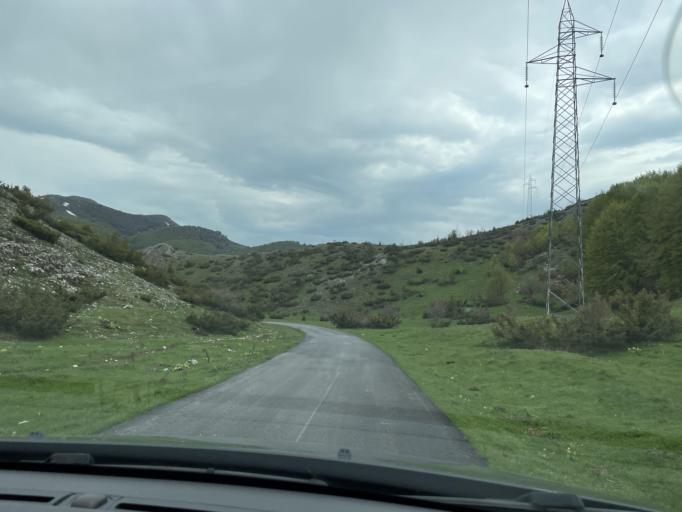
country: MK
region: Opstina Rostusa
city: Rostusha
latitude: 41.6092
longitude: 20.6806
